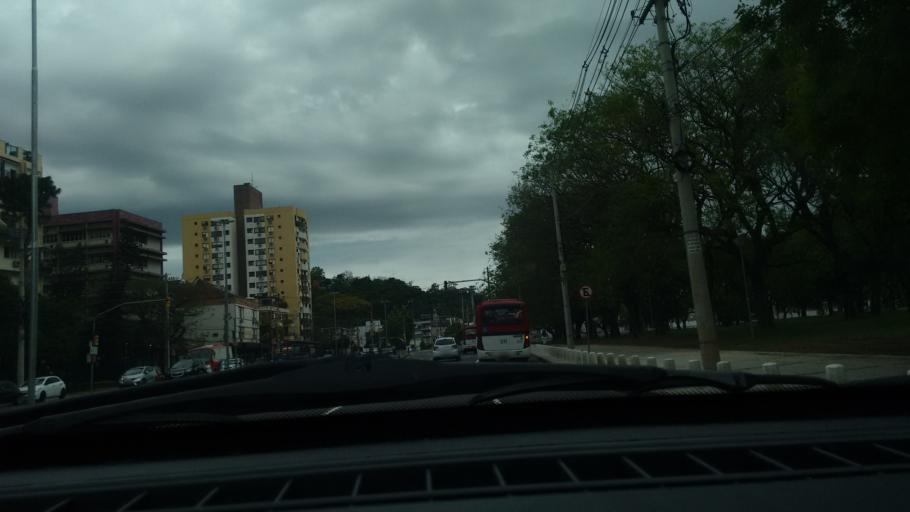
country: BR
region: Rio Grande do Sul
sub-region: Porto Alegre
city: Porto Alegre
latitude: -30.0619
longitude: -51.2313
